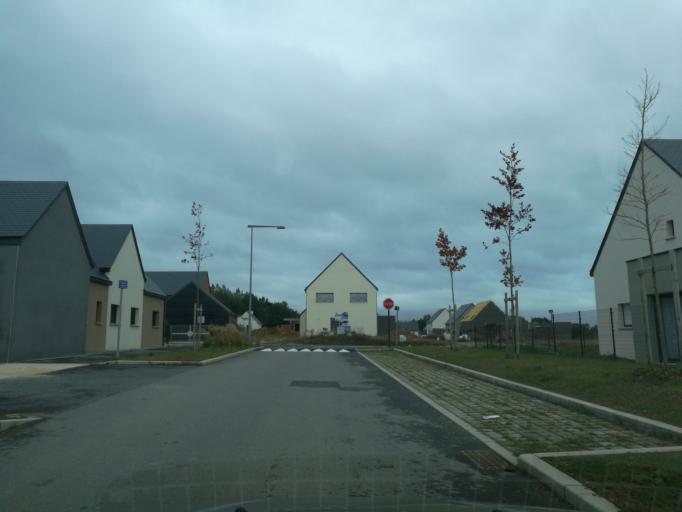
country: FR
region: Brittany
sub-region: Departement d'Ille-et-Vilaine
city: Pleumeleuc
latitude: 48.1834
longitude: -1.9110
